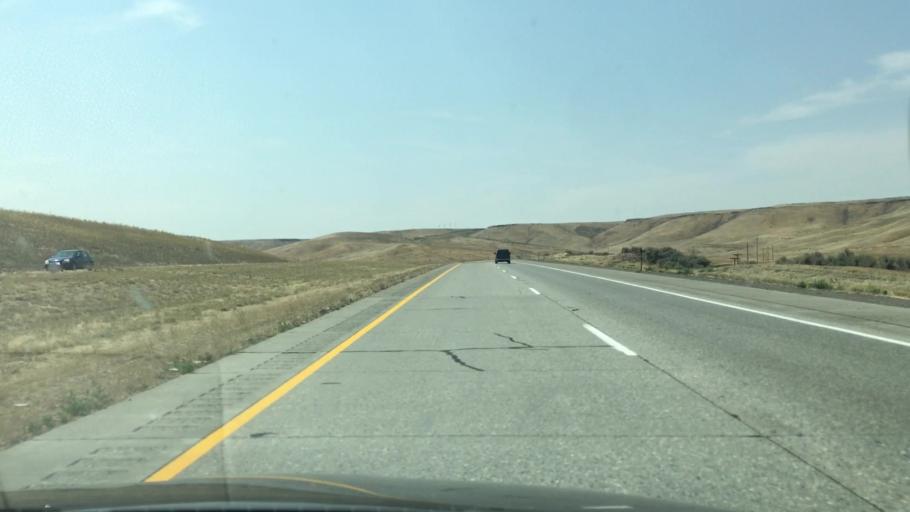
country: US
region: Idaho
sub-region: Elmore County
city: Glenns Ferry
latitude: 42.9642
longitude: -115.3261
